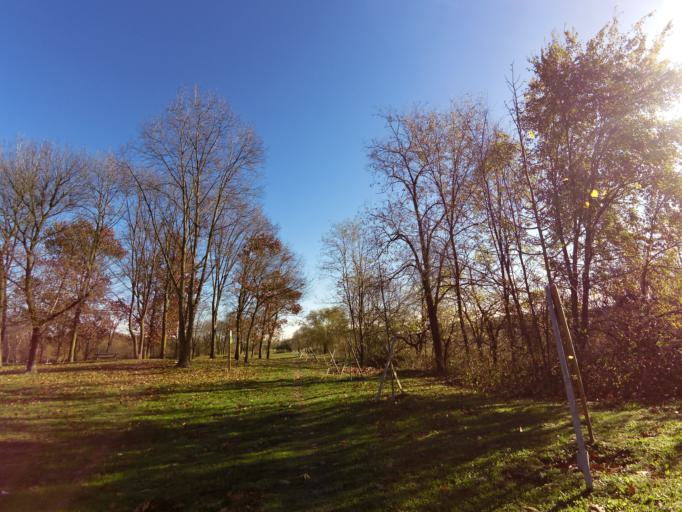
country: IT
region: Lombardy
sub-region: Citta metropolitana di Milano
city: Chiaravalle
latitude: 45.4325
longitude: 9.2323
